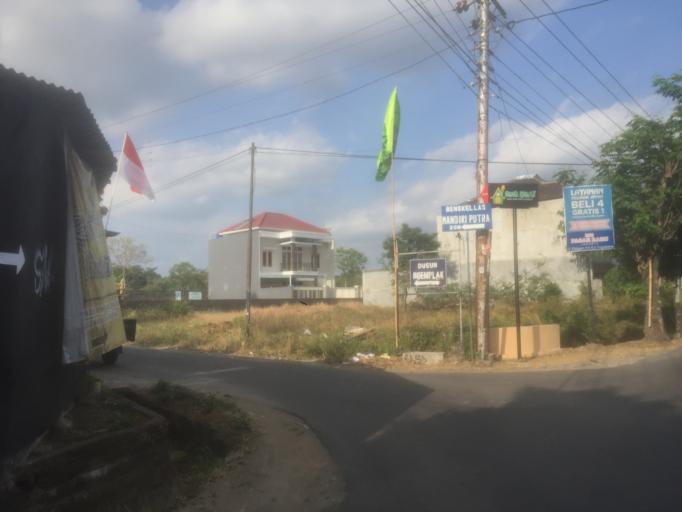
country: ID
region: Daerah Istimewa Yogyakarta
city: Melati
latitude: -7.7189
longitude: 110.3729
